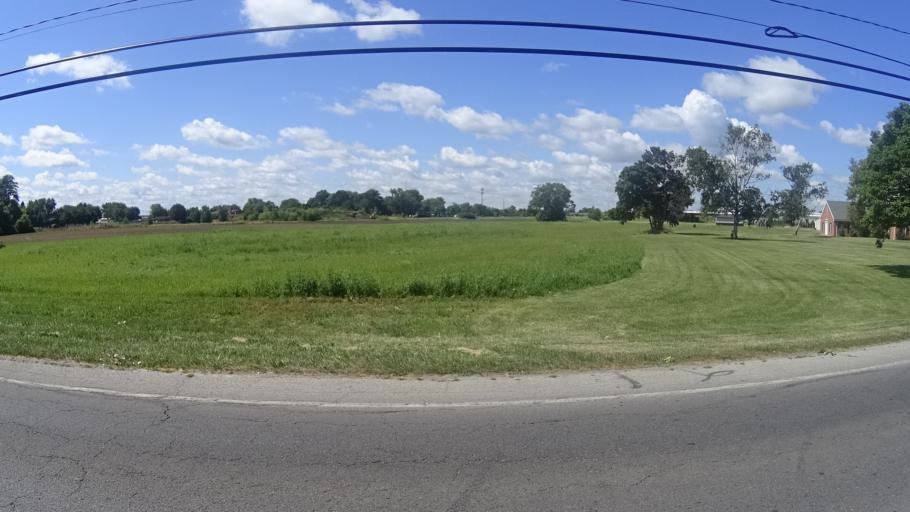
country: US
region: Ohio
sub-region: Erie County
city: Sandusky
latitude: 41.4297
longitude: -82.6706
